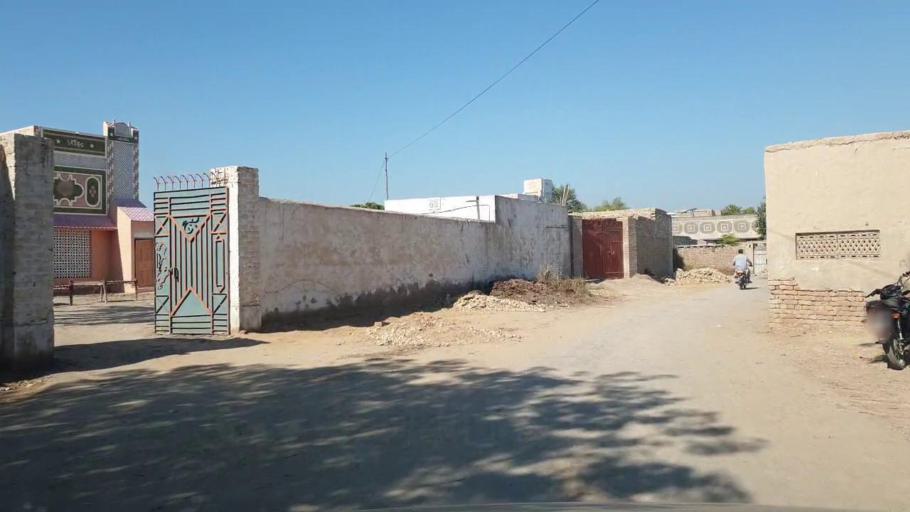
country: PK
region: Sindh
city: Shahpur Chakar
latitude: 26.1411
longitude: 68.6351
